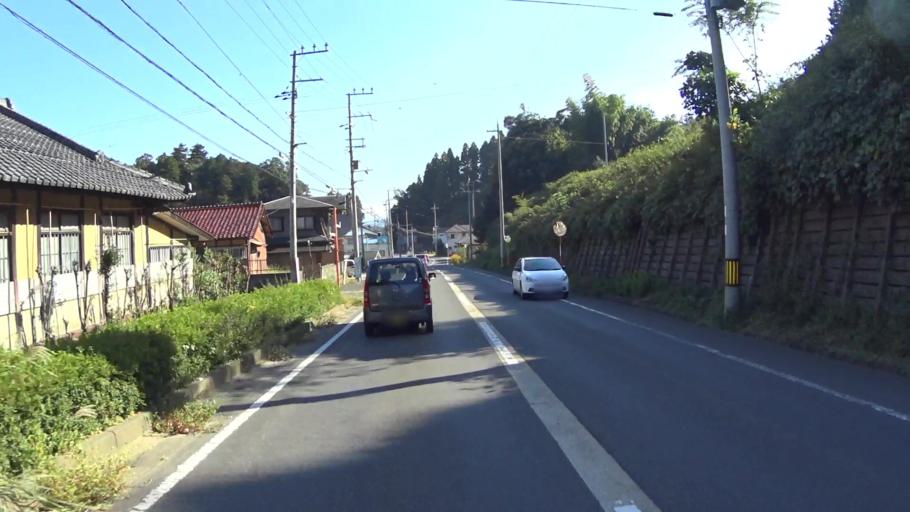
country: JP
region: Kyoto
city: Miyazu
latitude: 35.6328
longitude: 135.0543
